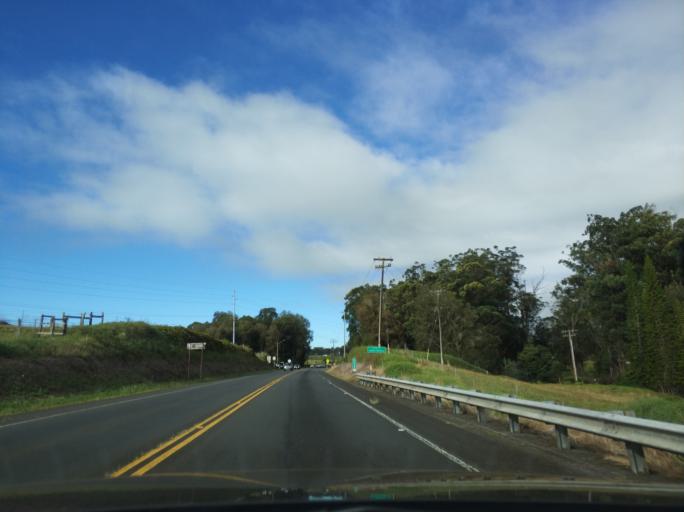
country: US
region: Hawaii
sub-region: Hawaii County
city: Waimea
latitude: 20.0431
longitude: -155.5955
